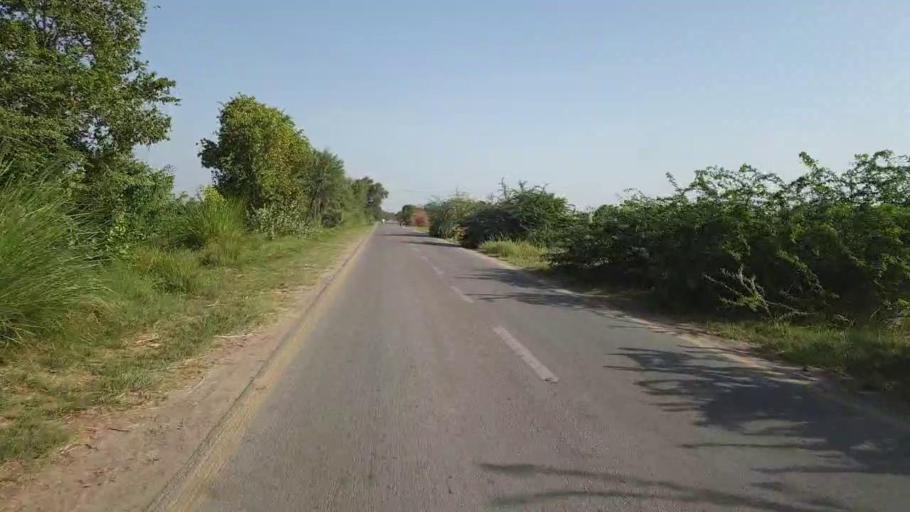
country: PK
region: Sindh
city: Daur
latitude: 26.4565
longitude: 68.4507
